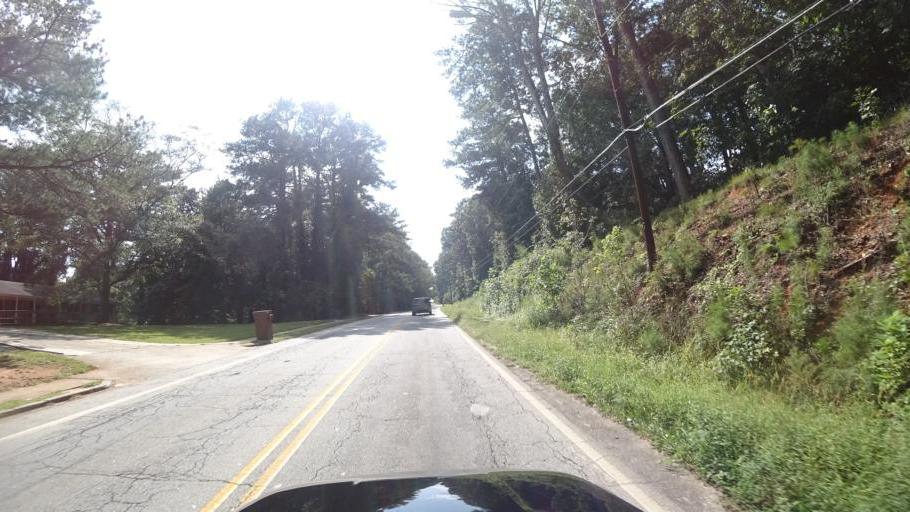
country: US
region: Georgia
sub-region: DeKalb County
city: Stone Mountain
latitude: 33.7882
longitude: -84.1892
